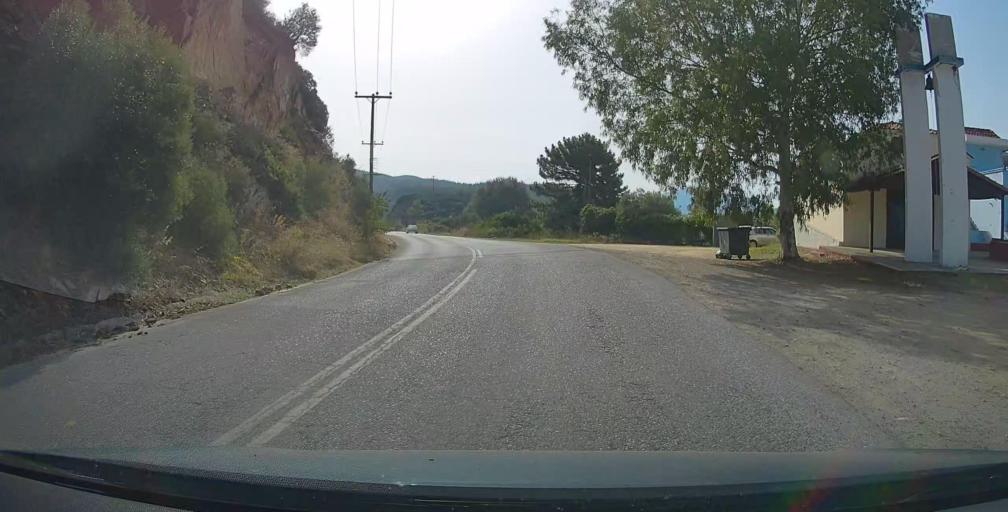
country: GR
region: Central Macedonia
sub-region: Nomos Chalkidikis
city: Sykia
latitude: 39.9709
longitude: 23.9200
